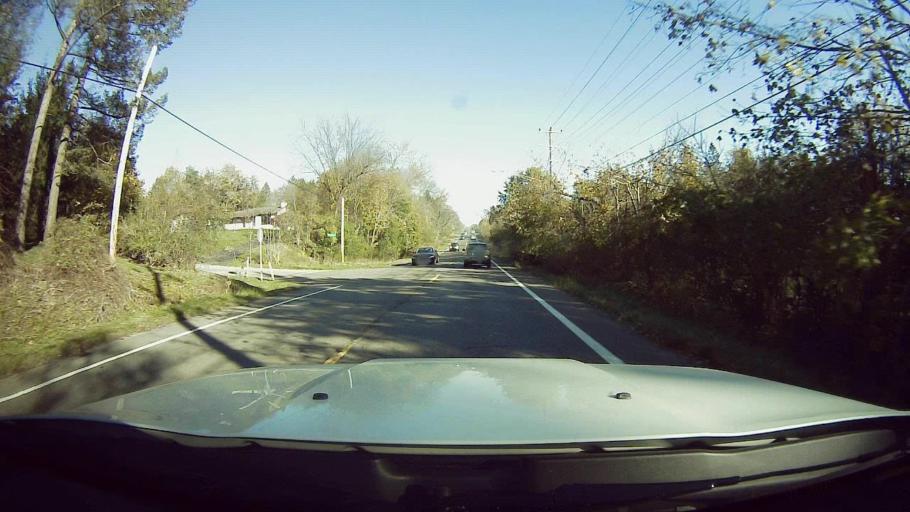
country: US
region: Michigan
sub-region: Oakland County
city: Franklin
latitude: 42.5441
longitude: -83.3148
